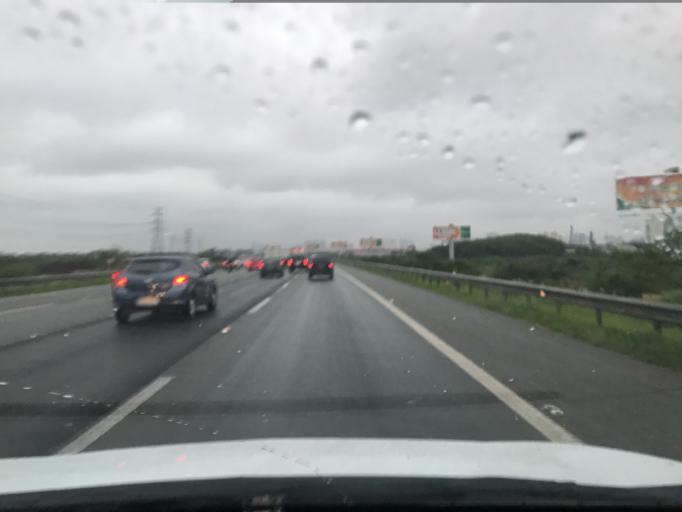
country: BR
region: Sao Paulo
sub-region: Guarulhos
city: Guarulhos
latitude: -23.4728
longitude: -46.5069
